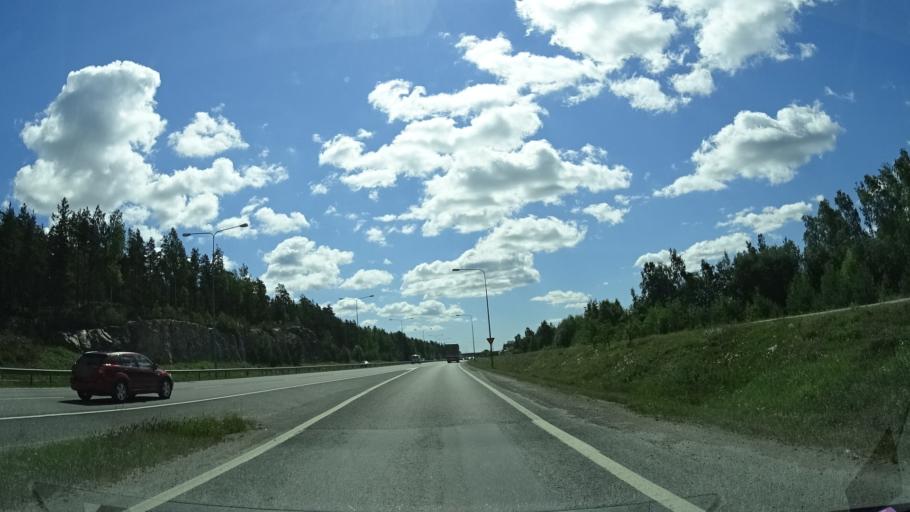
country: FI
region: Varsinais-Suomi
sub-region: Turku
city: Raisio
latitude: 60.5036
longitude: 22.1581
